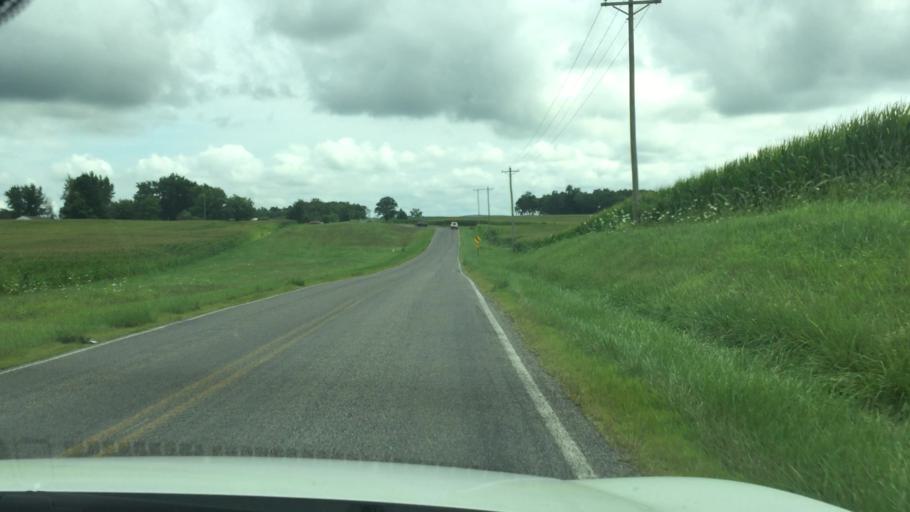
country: US
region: Ohio
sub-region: Champaign County
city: Mechanicsburg
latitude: 40.0498
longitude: -83.6566
